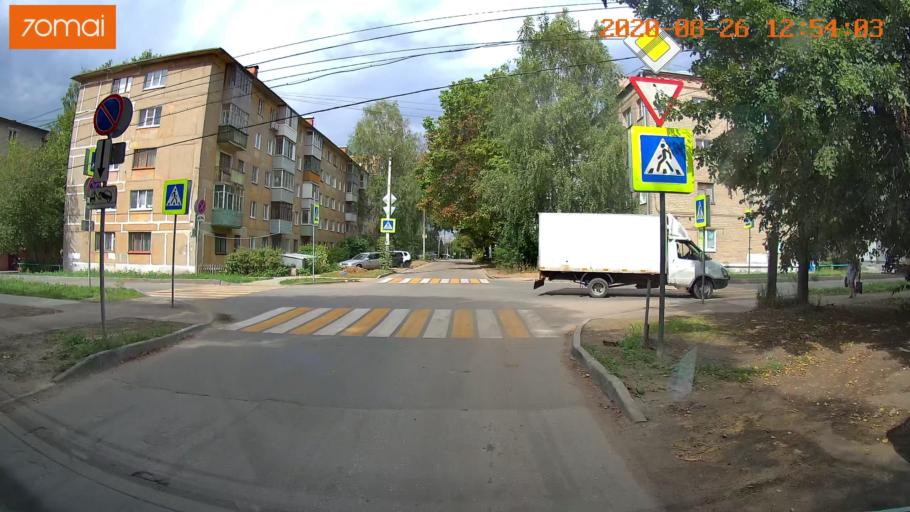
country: RU
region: Rjazan
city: Ryazan'
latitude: 54.6030
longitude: 39.7592
